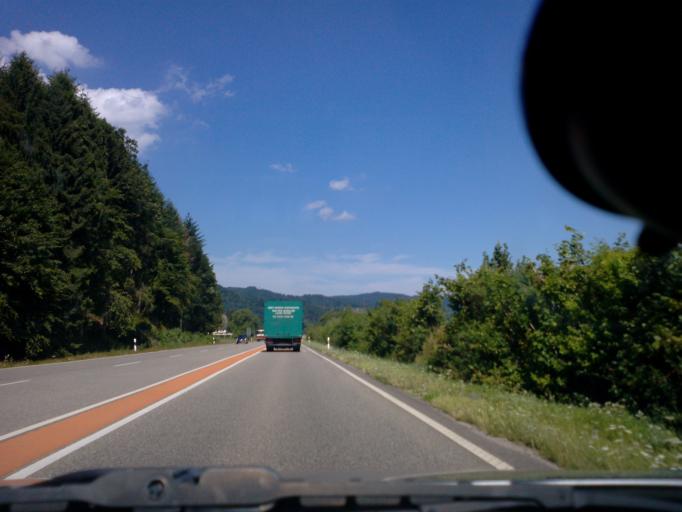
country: DE
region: Baden-Wuerttemberg
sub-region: Freiburg Region
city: Biberach
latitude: 48.3252
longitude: 8.0318
